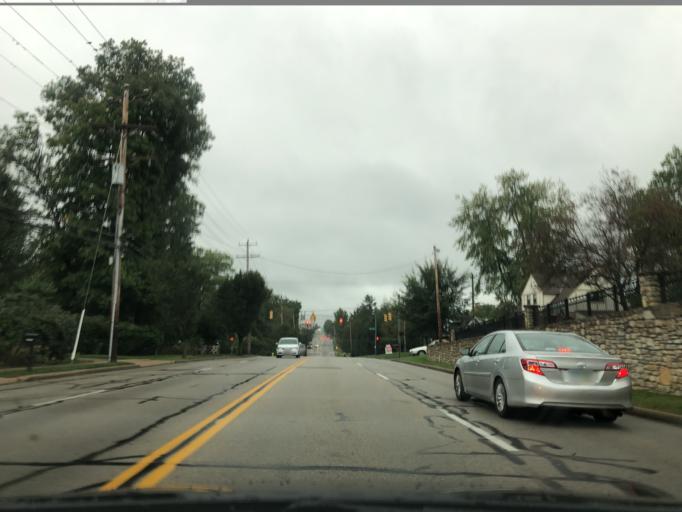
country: US
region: Ohio
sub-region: Hamilton County
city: Rossmoyne
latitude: 39.2121
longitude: -84.3791
